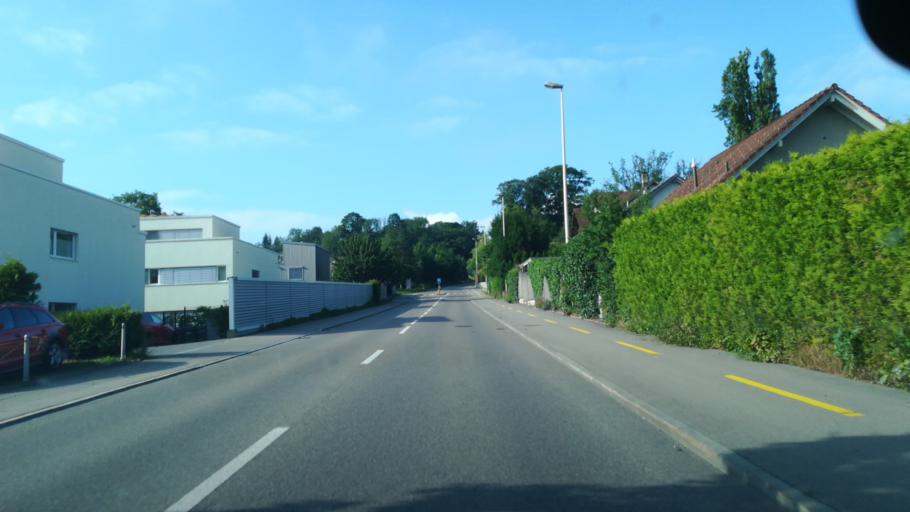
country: CH
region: Thurgau
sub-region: Kreuzlingen District
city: Kreuzlingen
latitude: 47.6388
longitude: 9.1662
